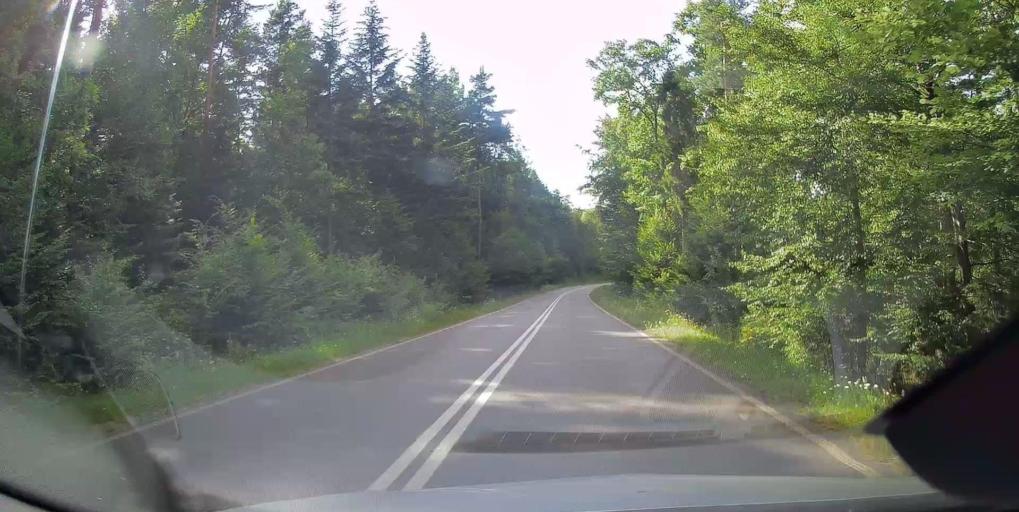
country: PL
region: Swietokrzyskie
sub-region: Powiat skarzyski
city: Laczna
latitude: 50.9952
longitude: 20.8548
